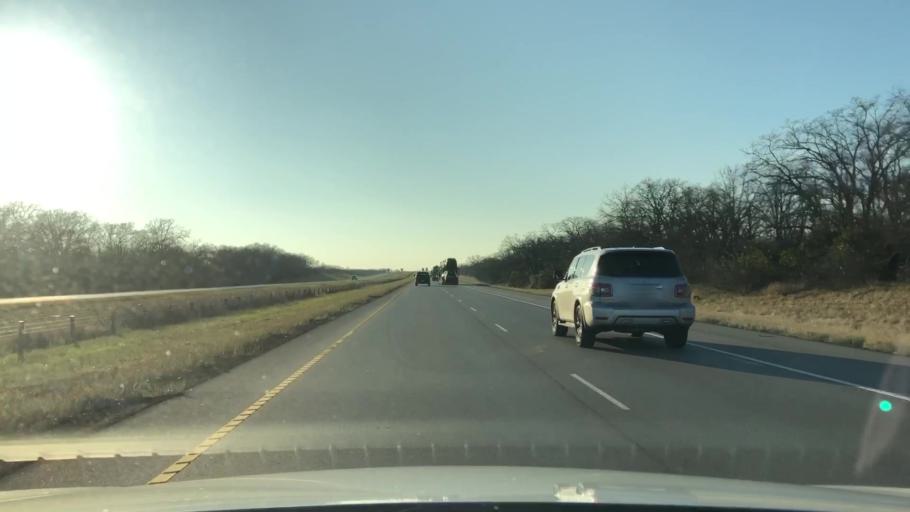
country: US
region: Texas
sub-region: Gonzales County
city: Gonzales
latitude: 29.6514
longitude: -97.4737
